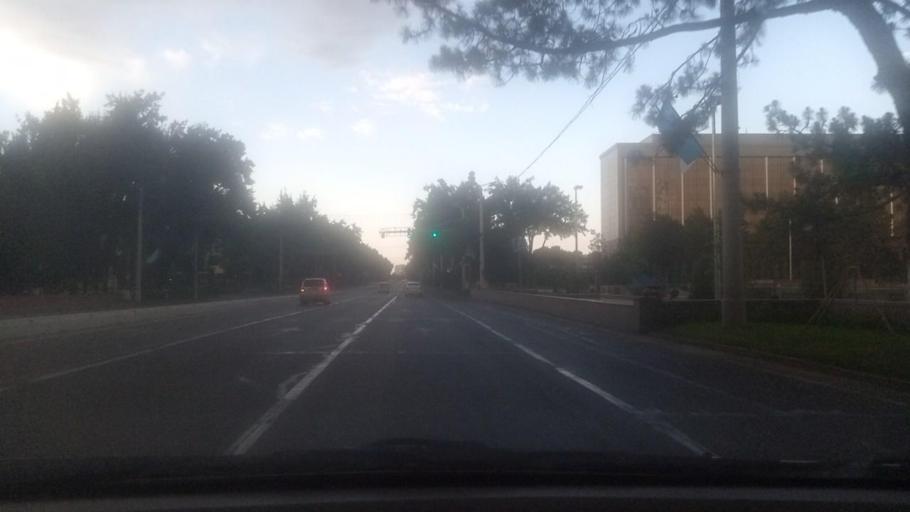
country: UZ
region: Toshkent Shahri
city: Tashkent
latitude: 41.3138
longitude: 69.2694
